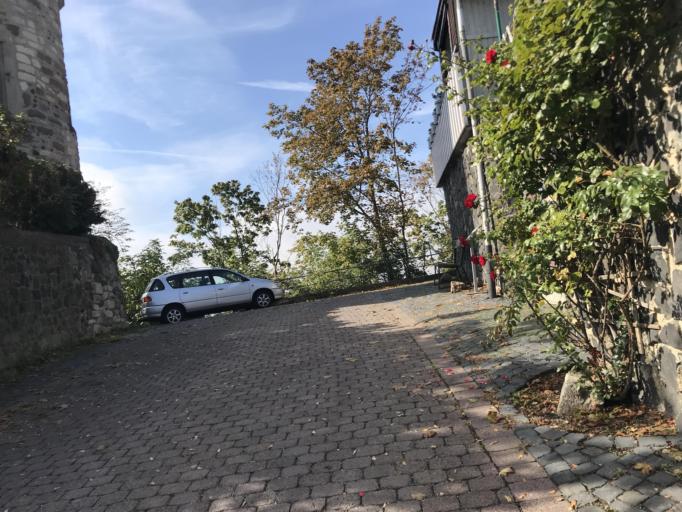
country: DE
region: Hesse
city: Gudensberg
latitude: 51.1764
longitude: 9.3658
